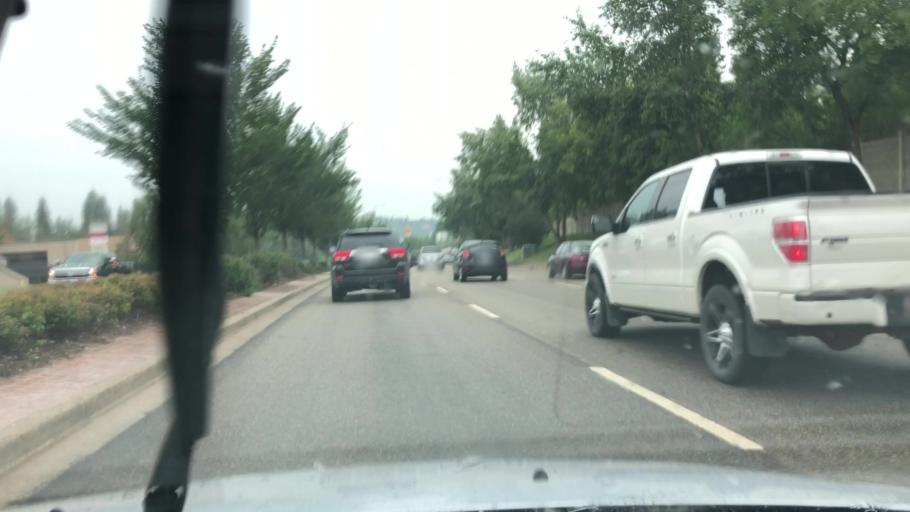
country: CA
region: Alberta
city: St. Albert
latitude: 53.6287
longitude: -113.6199
